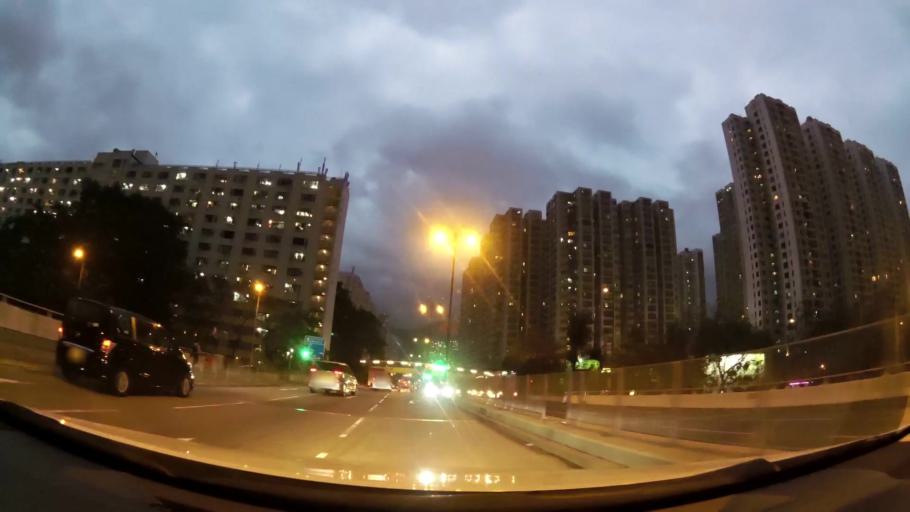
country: HK
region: Sha Tin
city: Sha Tin
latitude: 22.3848
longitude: 114.1896
